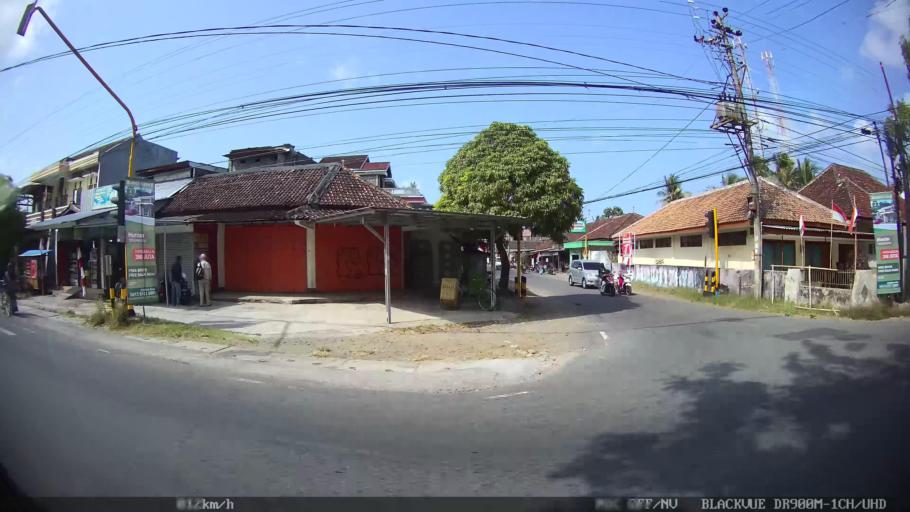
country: ID
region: Daerah Istimewa Yogyakarta
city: Srandakan
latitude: -7.8938
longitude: 110.1434
